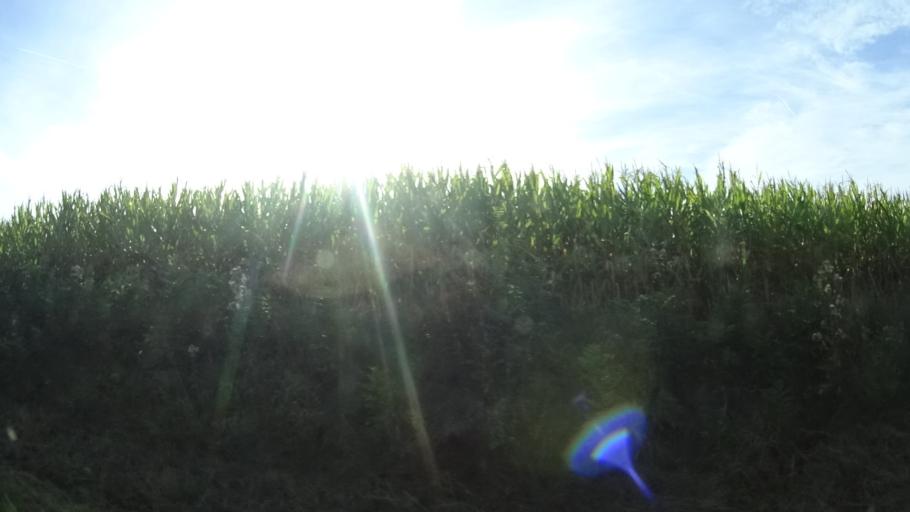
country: DE
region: Hesse
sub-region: Regierungsbezirk Kassel
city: Kunzell
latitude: 50.5344
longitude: 9.7509
